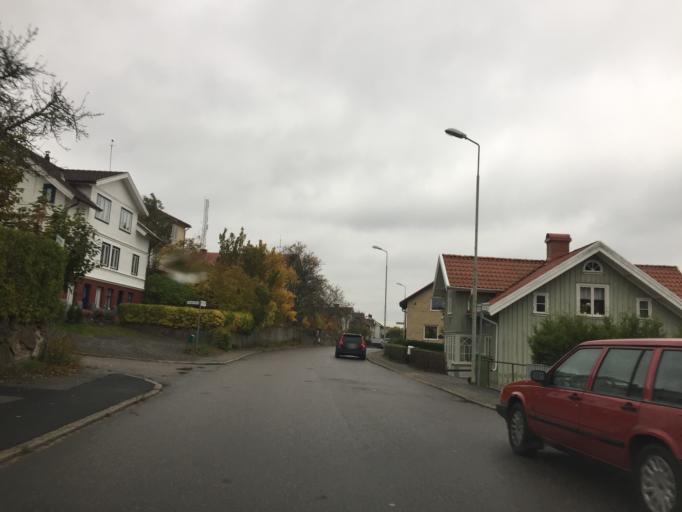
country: SE
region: Vaestra Goetaland
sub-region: Trollhattan
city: Trollhattan
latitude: 58.2832
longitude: 12.2740
